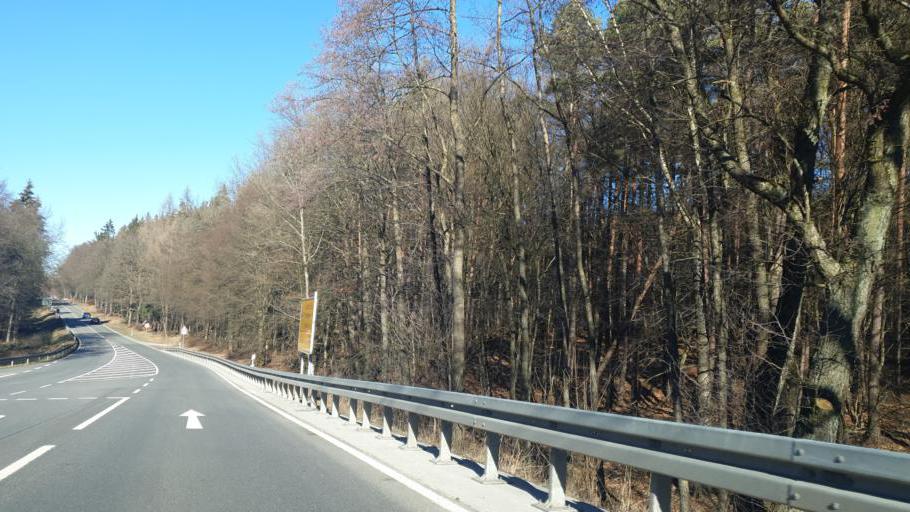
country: DE
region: Hesse
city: Taunusstein
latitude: 50.1462
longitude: 8.2162
